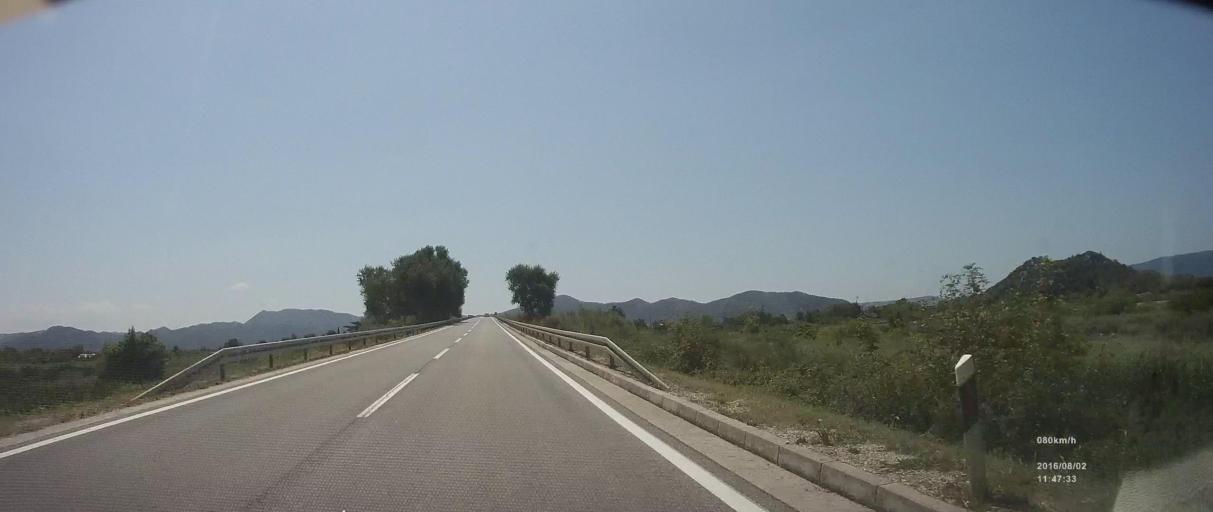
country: HR
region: Dubrovacko-Neretvanska
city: Komin
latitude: 43.0426
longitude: 17.4828
